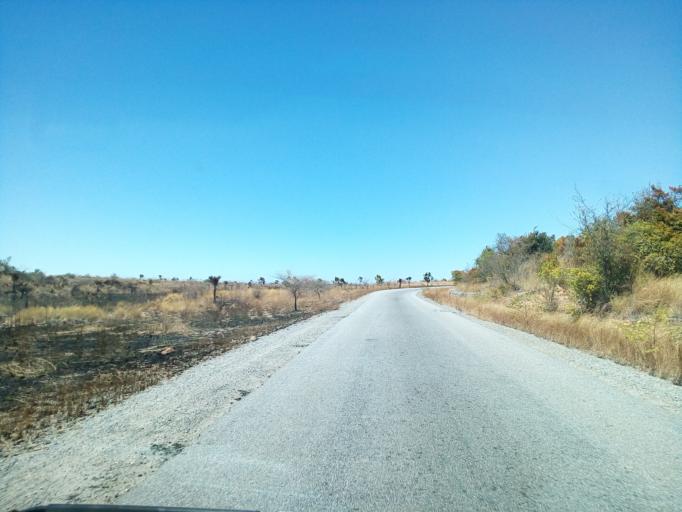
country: MG
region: Betsiboka
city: Maevatanana
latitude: -16.6383
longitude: 47.0893
